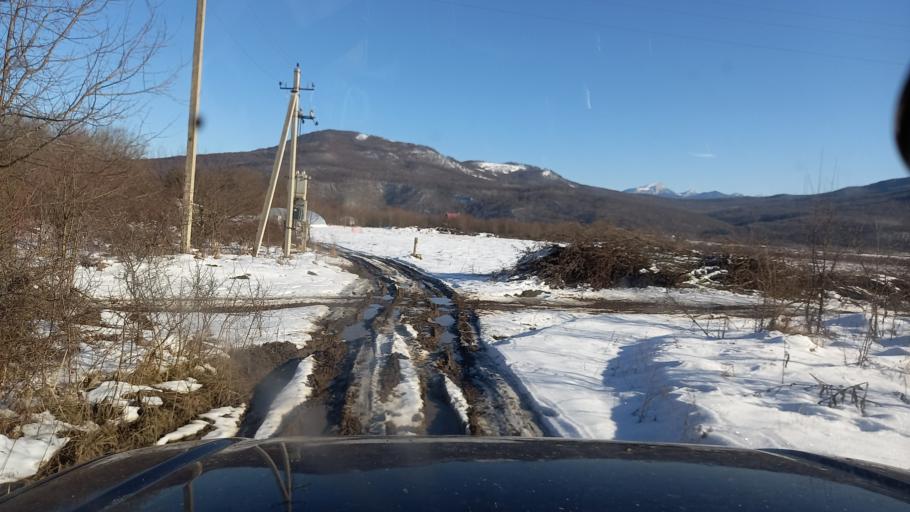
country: RU
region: Adygeya
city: Kamennomostskiy
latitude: 44.2028
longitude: 40.1509
